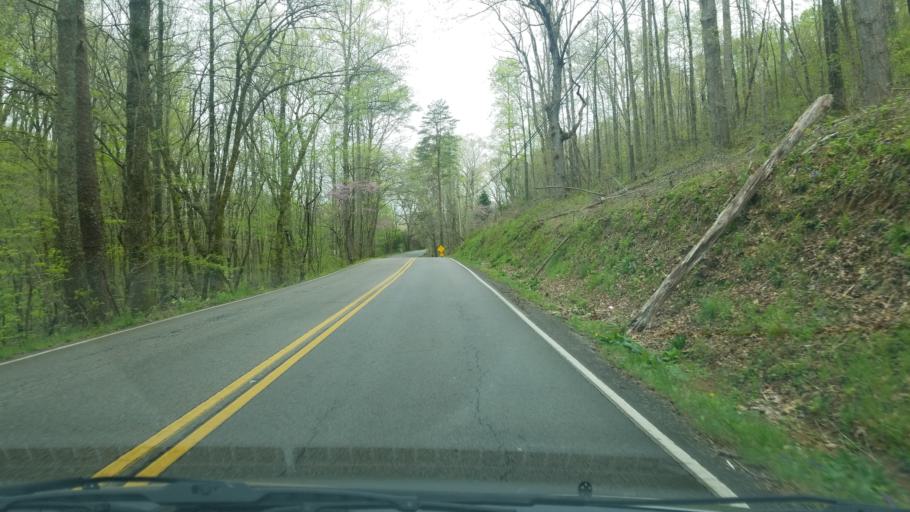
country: US
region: Tennessee
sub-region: Hamilton County
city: Collegedale
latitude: 35.0087
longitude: -85.0785
